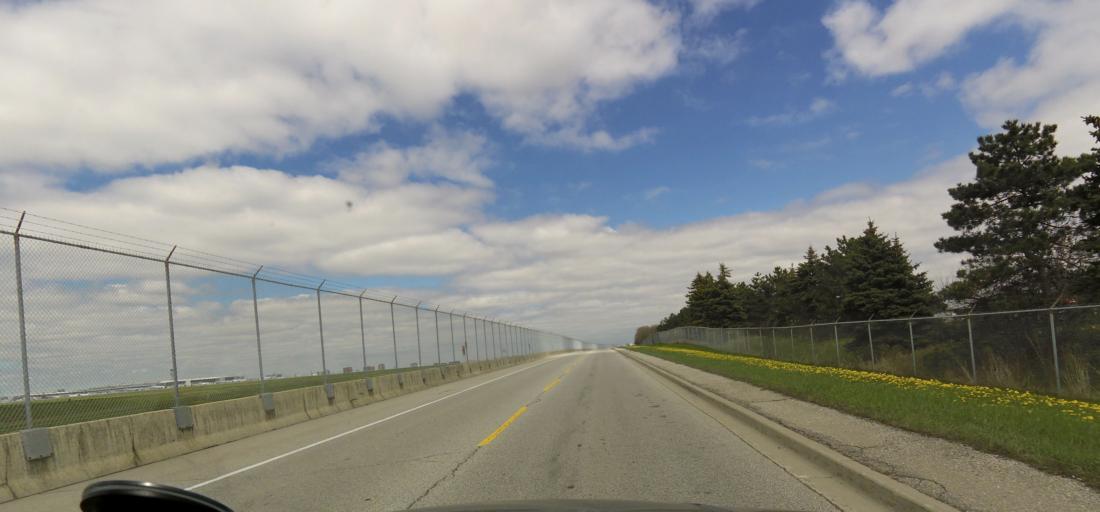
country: CA
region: Ontario
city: Etobicoke
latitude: 43.6588
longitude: -79.6180
